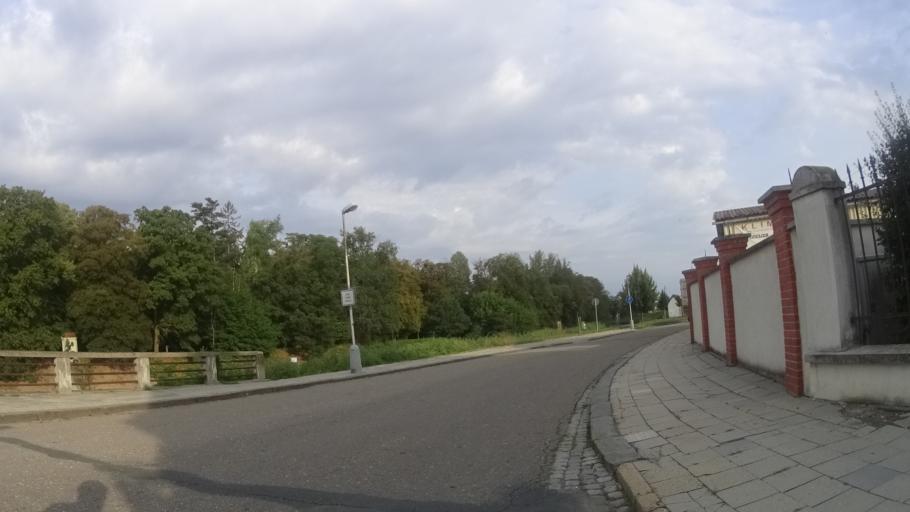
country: CZ
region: Zlin
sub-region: Okres Kromeriz
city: Kromeriz
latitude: 49.3024
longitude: 17.3997
